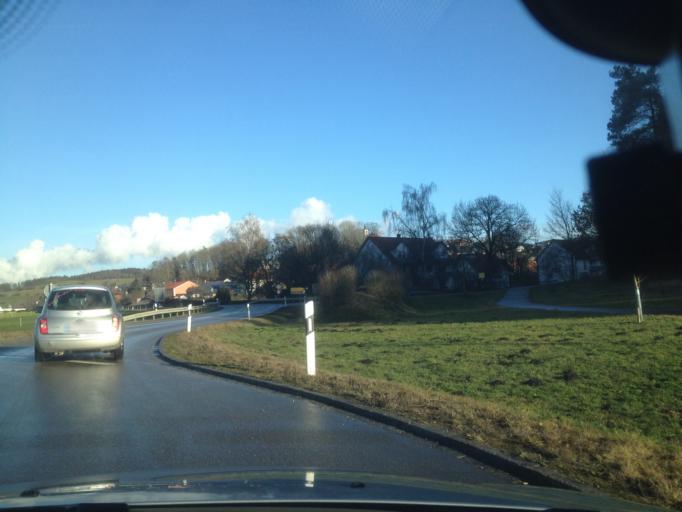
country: DE
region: Bavaria
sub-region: Swabia
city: Burgau
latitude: 48.4435
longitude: 10.4272
